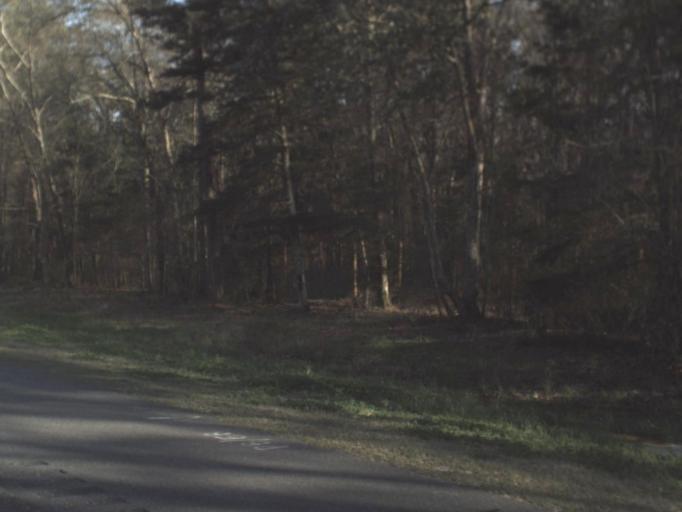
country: US
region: Florida
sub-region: Gadsden County
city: Midway
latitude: 30.4929
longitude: -84.4370
